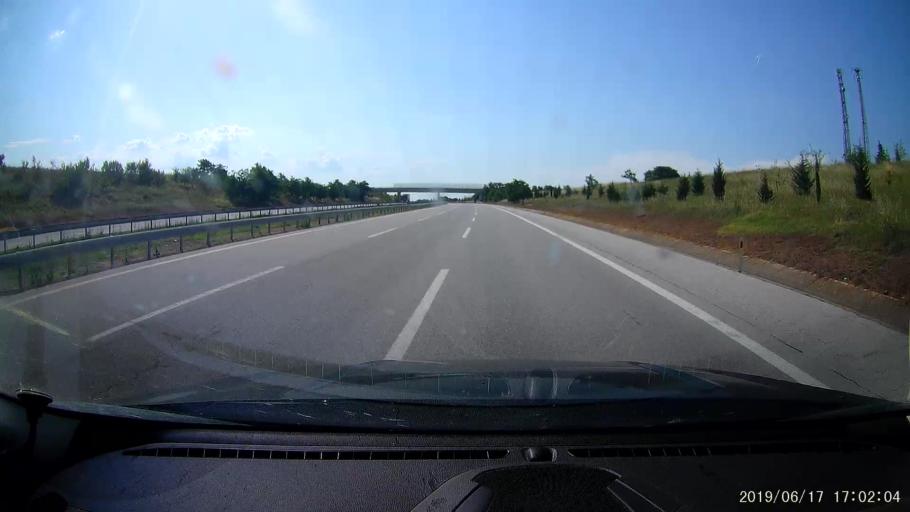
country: TR
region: Edirne
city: Haskoy
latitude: 41.6357
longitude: 26.7902
